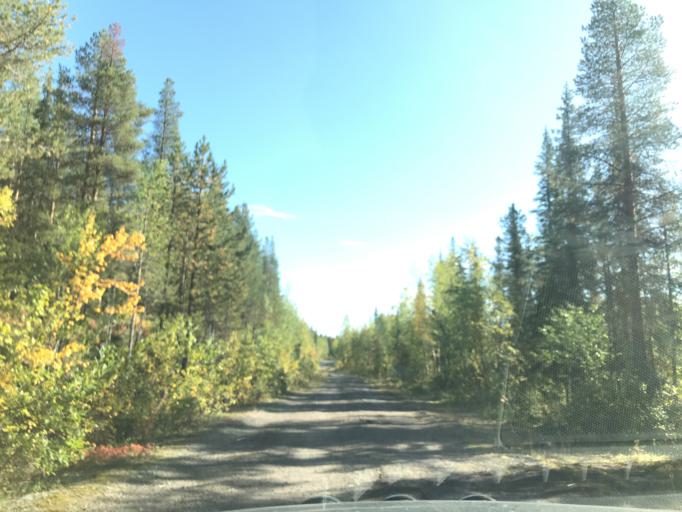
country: SE
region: Norrbotten
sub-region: Gallivare Kommun
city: Malmberget
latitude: 67.6459
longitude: 21.1071
